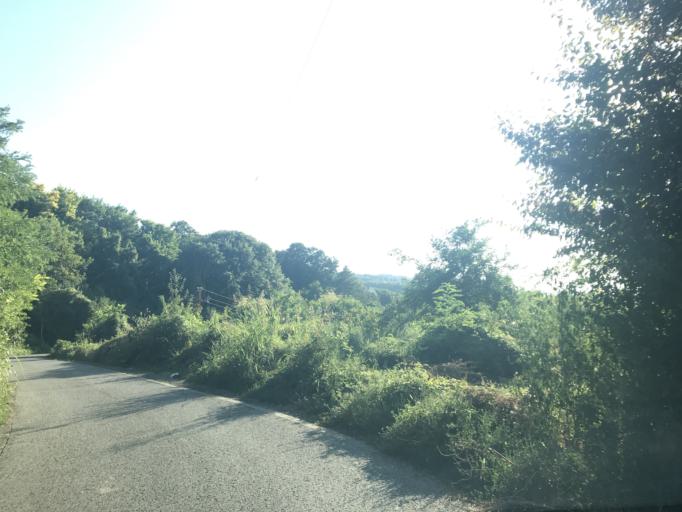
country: RS
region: Autonomna Pokrajina Vojvodina
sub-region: Juznobacki Okrug
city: Novi Sad
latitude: 45.2136
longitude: 19.8030
